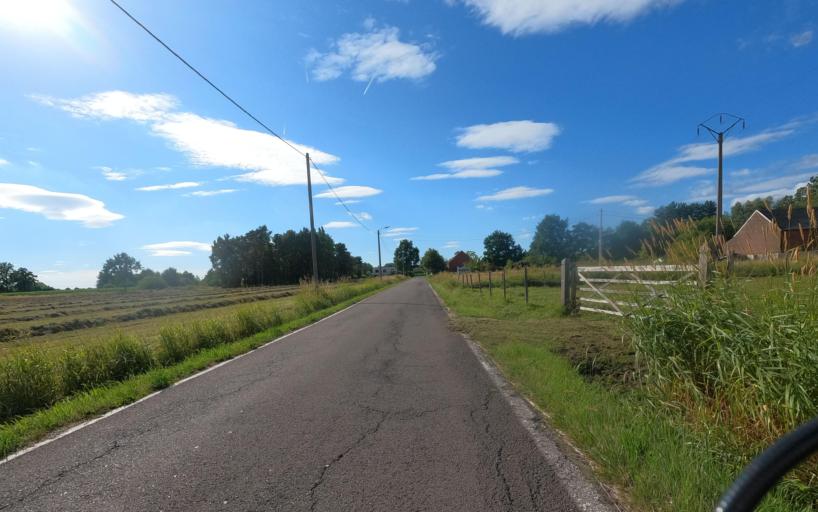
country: BE
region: Flanders
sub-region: Provincie Antwerpen
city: Heist-op-den-Berg
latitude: 51.0382
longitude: 4.7199
